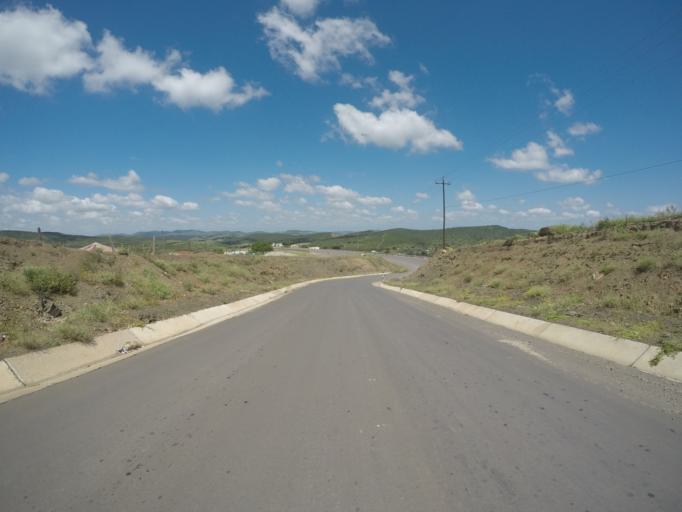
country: ZA
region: KwaZulu-Natal
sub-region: uThungulu District Municipality
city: Empangeni
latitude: -28.6101
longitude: 31.7470
